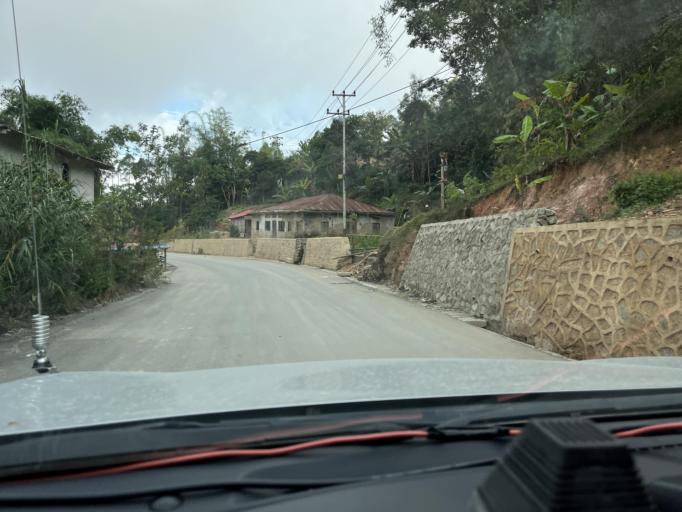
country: TL
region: Dili
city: Dili
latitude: -8.6374
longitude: 125.6131
